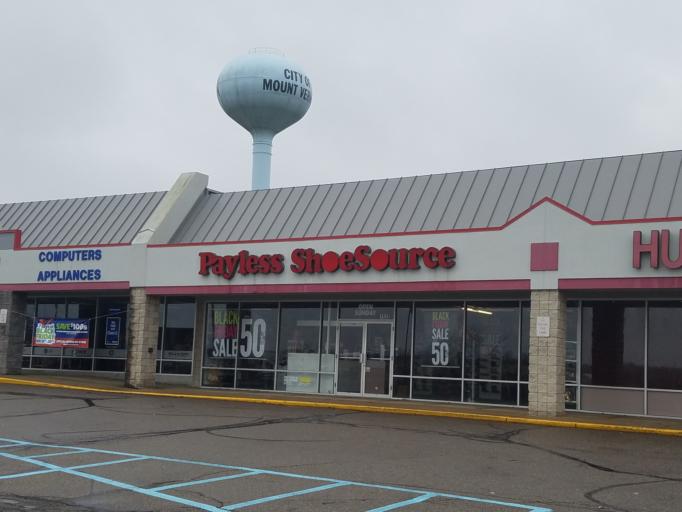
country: US
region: Ohio
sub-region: Knox County
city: Mount Vernon
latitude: 40.4006
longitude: -82.4445
